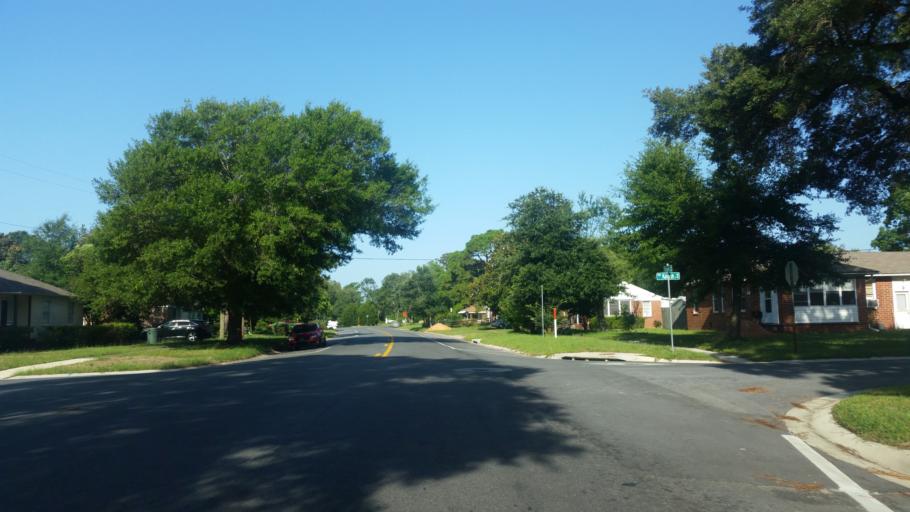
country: US
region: Florida
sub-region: Escambia County
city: Warrington
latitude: 30.3805
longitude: -87.2866
